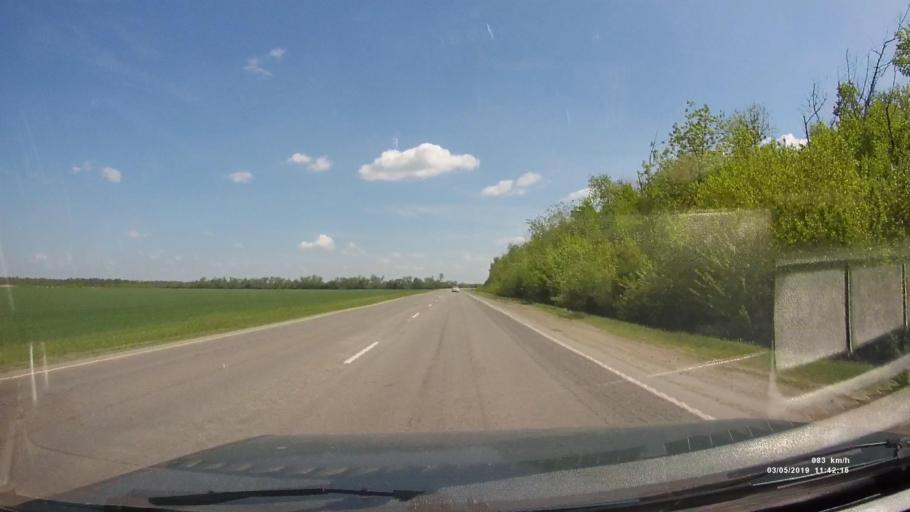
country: RU
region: Rostov
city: Starocherkasskaya
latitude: 47.1380
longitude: 40.0397
